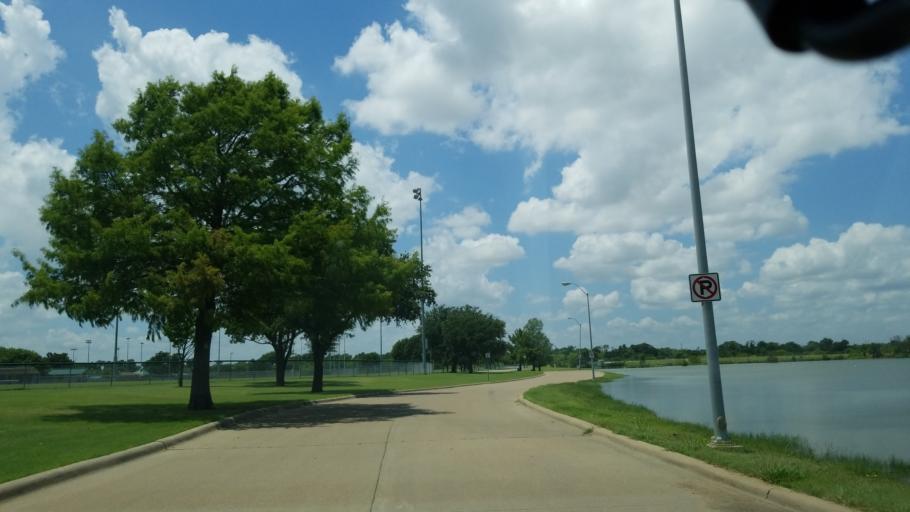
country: US
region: Texas
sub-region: Dallas County
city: Carrollton
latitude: 32.9596
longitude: -96.9372
